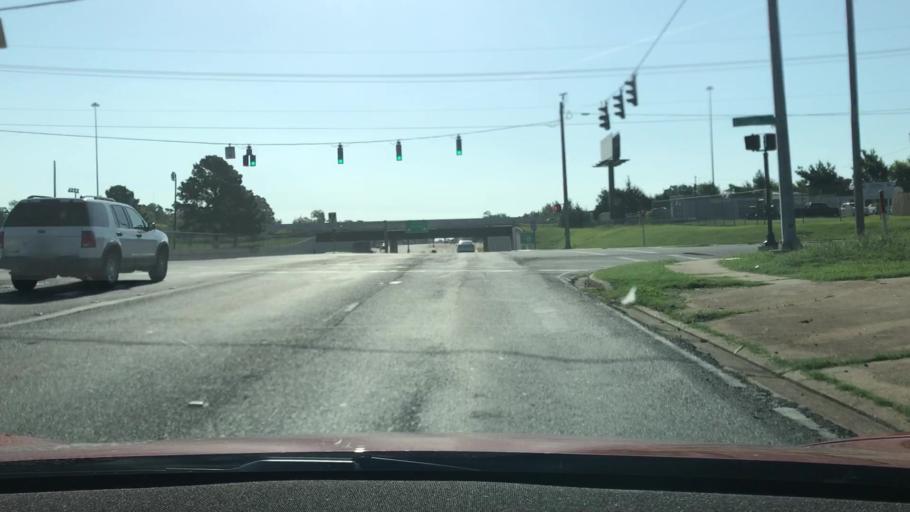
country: US
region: Louisiana
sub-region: Bossier Parish
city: Bossier City
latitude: 32.4418
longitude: -93.7592
